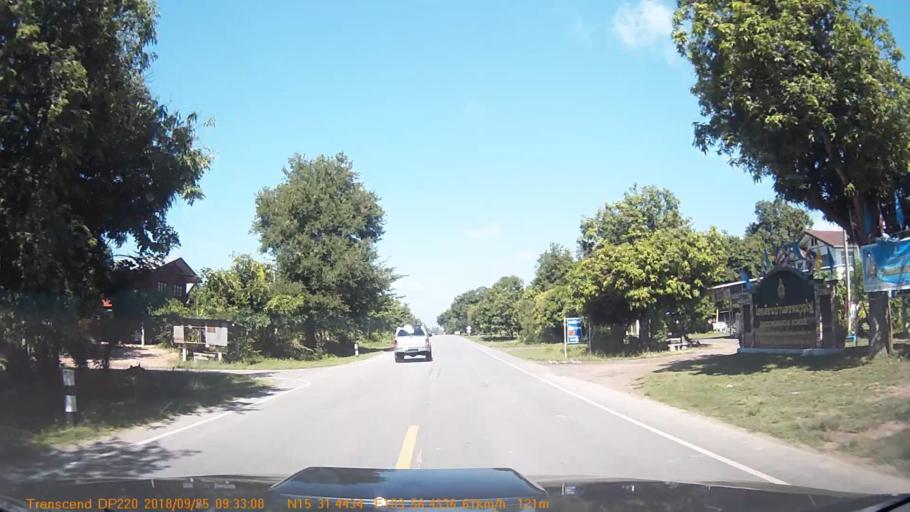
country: TH
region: Roi Et
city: Phon Sai
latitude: 15.5240
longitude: 103.9408
